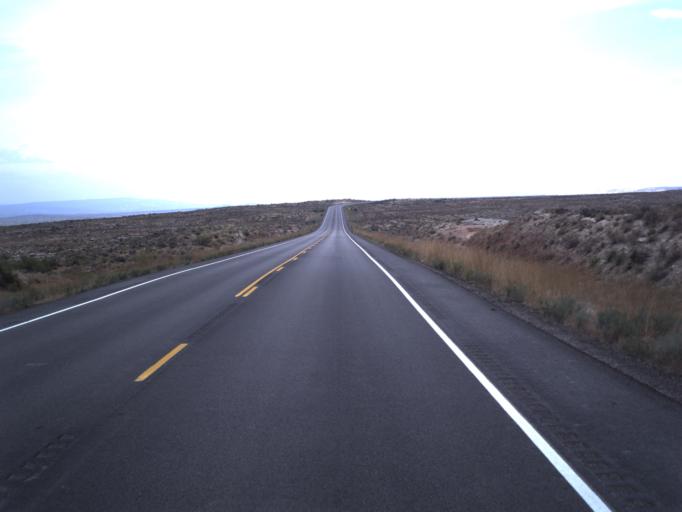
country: US
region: Utah
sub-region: Uintah County
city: Naples
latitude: 40.2624
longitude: -109.4468
